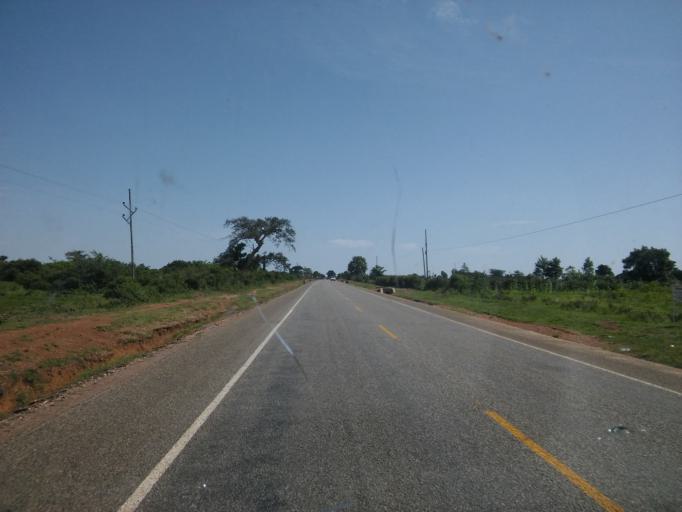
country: UG
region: Eastern Region
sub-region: Kumi District
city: Kumi
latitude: 1.3994
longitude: 34.0012
